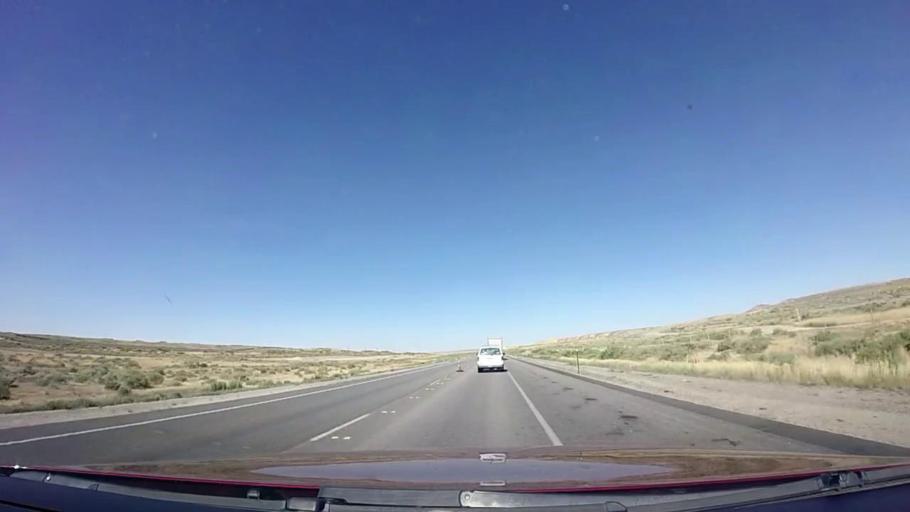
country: US
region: Wyoming
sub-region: Carbon County
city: Rawlins
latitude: 41.7062
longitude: -107.8577
